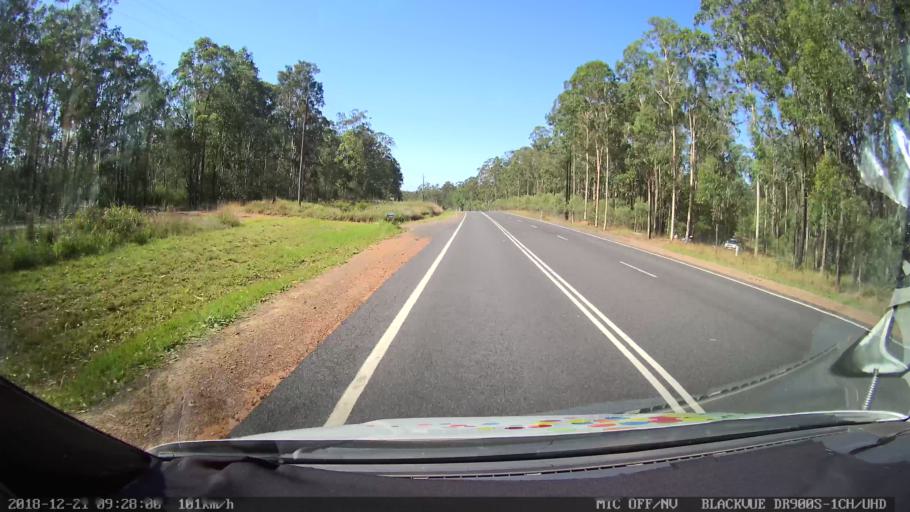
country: AU
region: New South Wales
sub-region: Clarence Valley
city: Maclean
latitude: -29.4109
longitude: 152.9874
